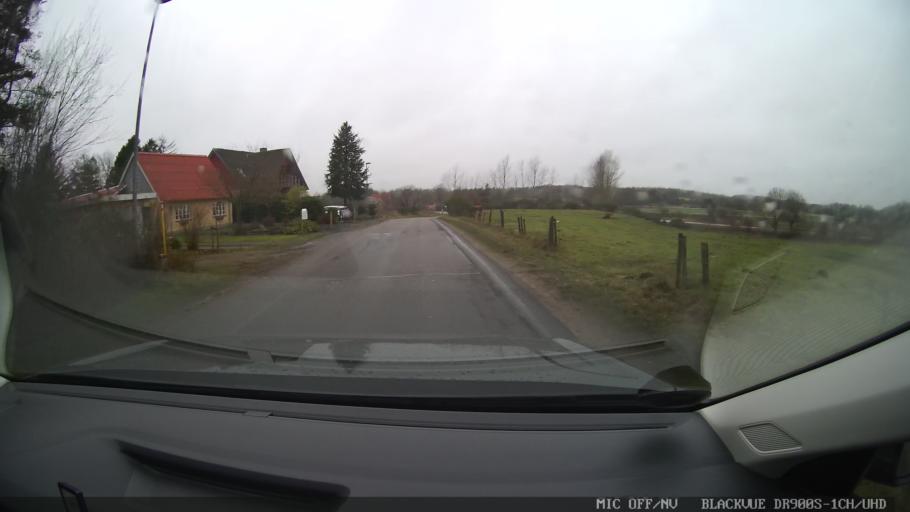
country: DK
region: Central Jutland
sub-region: Viborg Kommune
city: Karup
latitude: 56.2956
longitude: 9.1519
